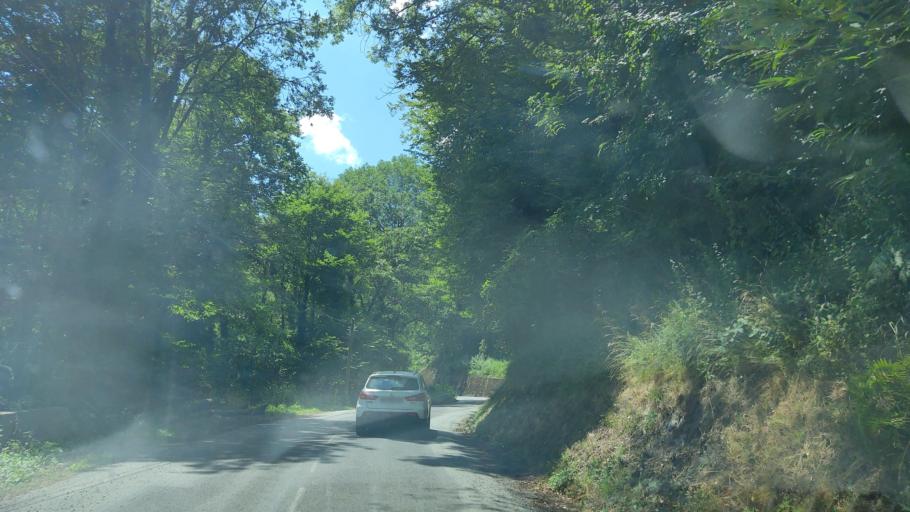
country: FR
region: Rhone-Alpes
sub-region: Departement de la Savoie
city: Aiton
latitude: 45.5125
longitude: 6.2963
